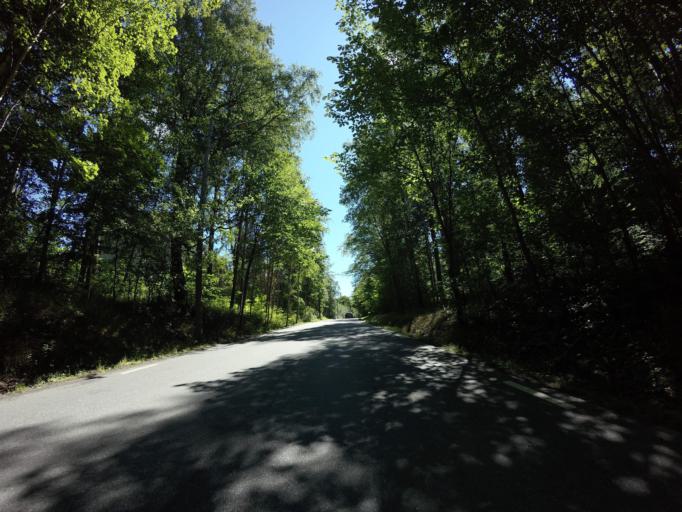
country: SE
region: Stockholm
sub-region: Lidingo
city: Lidingoe
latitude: 59.3380
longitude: 18.1328
